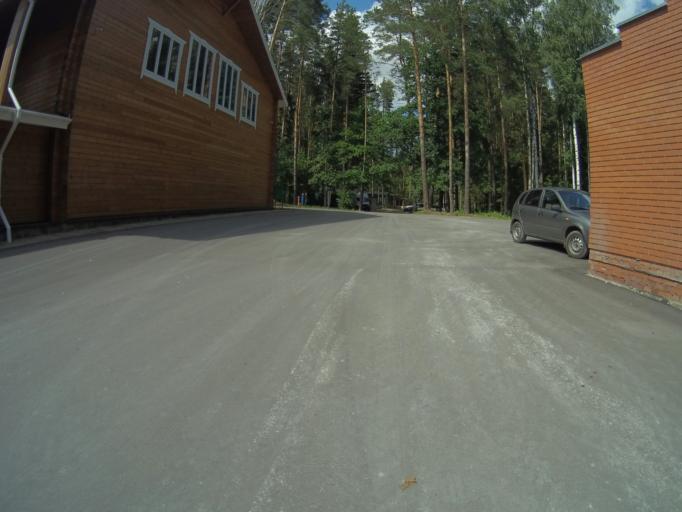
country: RU
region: Vladimir
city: Raduzhnyy
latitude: 56.0507
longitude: 40.2801
